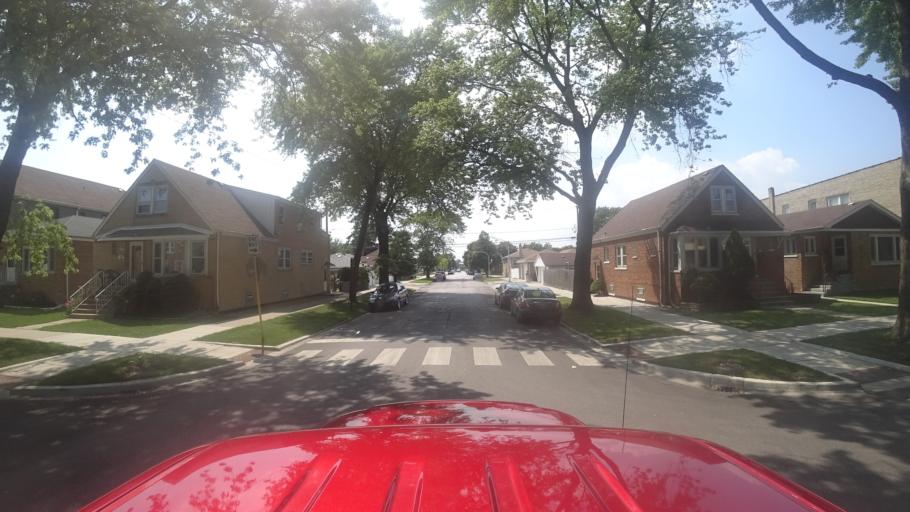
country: US
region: Illinois
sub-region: Cook County
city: Cicero
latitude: 41.8023
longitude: -87.7319
